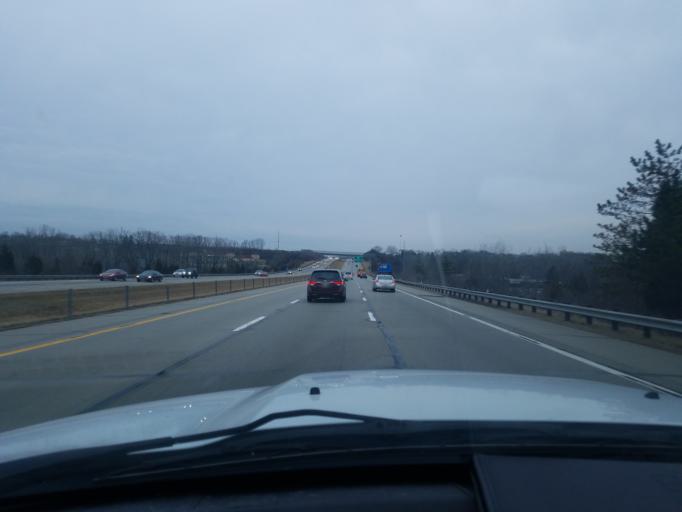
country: US
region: Ohio
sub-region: Montgomery County
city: Centerville
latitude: 39.6506
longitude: -84.1418
